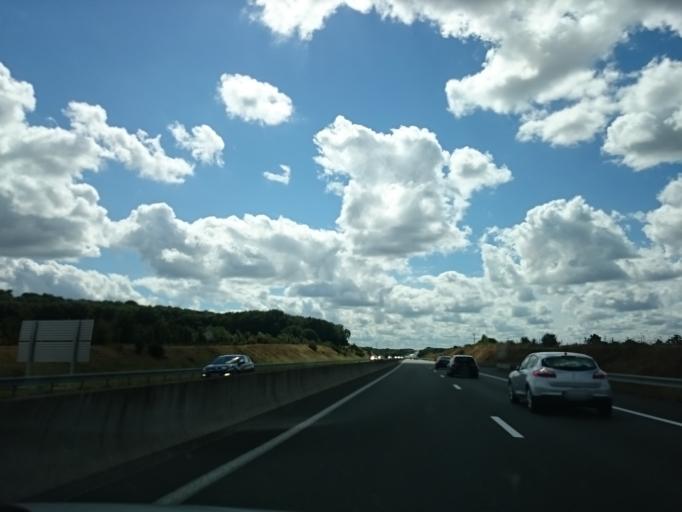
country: FR
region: Pays de la Loire
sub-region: Departement de Maine-et-Loire
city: Saint-Lambert-la-Potherie
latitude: 47.4851
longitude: -0.6610
